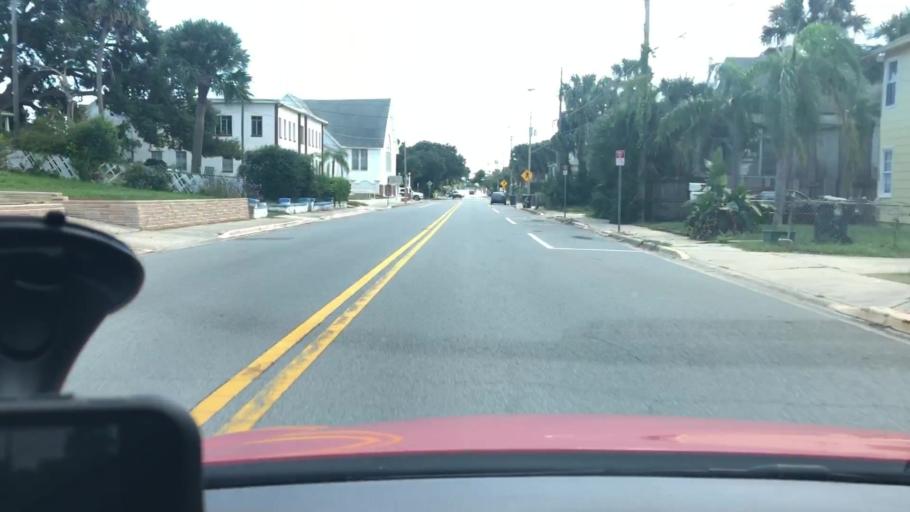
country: US
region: Florida
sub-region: Volusia County
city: Daytona Beach
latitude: 29.2292
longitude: -81.0150
